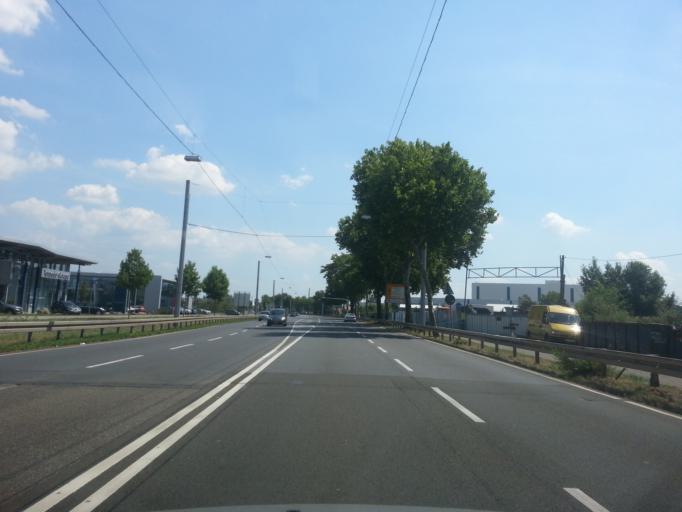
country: DE
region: Baden-Wuerttemberg
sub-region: Karlsruhe Region
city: Mannheim
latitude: 49.5412
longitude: 8.4634
